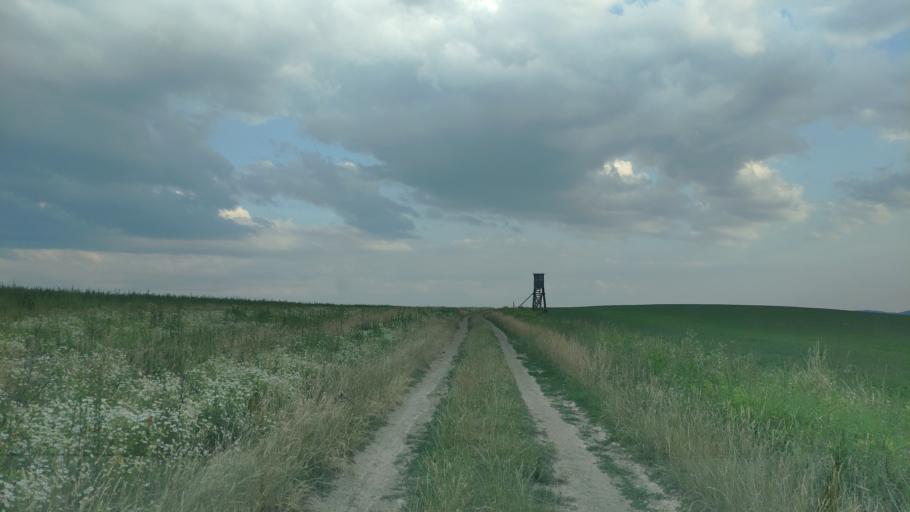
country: SK
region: Kosicky
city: Moldava nad Bodvou
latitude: 48.6930
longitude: 20.9891
